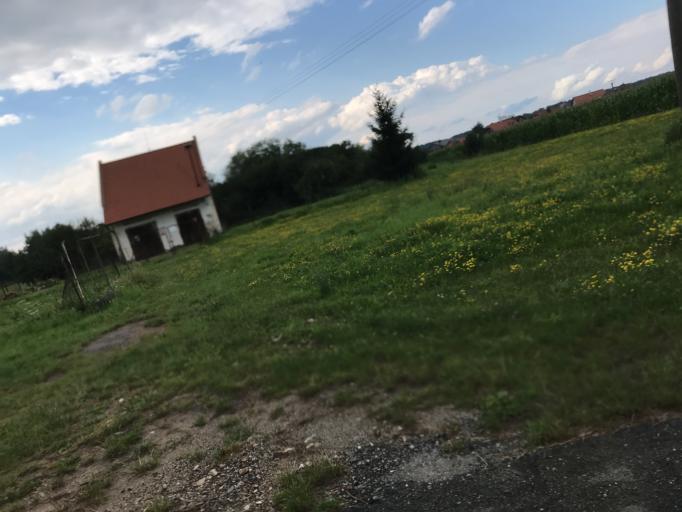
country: CZ
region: Jihocesky
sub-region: Okres Jindrichuv Hradec
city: Trebon
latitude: 49.0129
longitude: 14.7491
